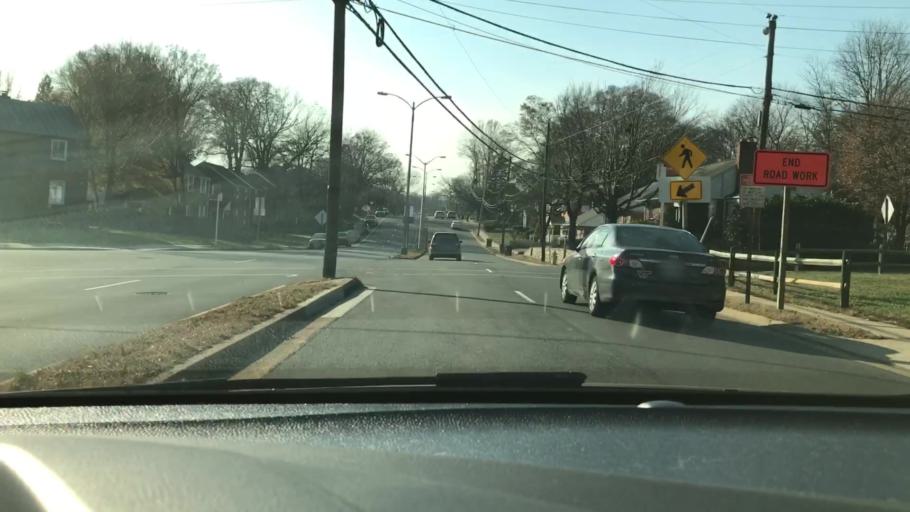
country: US
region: Virginia
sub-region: Arlington County
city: Arlington
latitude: 38.8735
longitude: -77.1183
